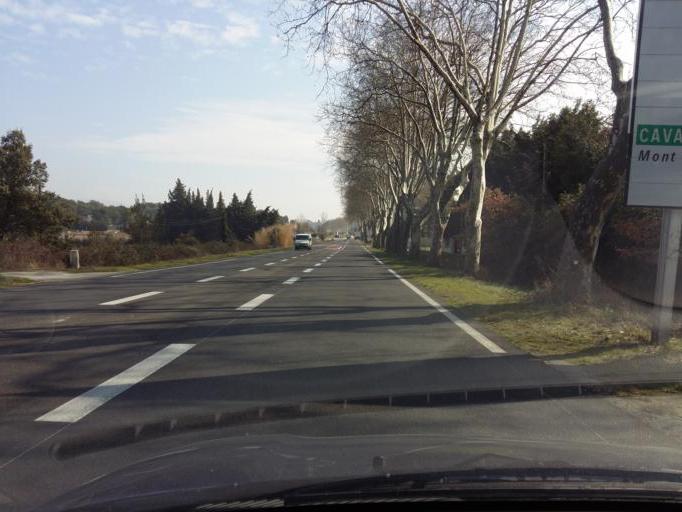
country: FR
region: Provence-Alpes-Cote d'Azur
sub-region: Departement des Bouches-du-Rhone
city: Orgon
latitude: 43.7937
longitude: 5.0249
